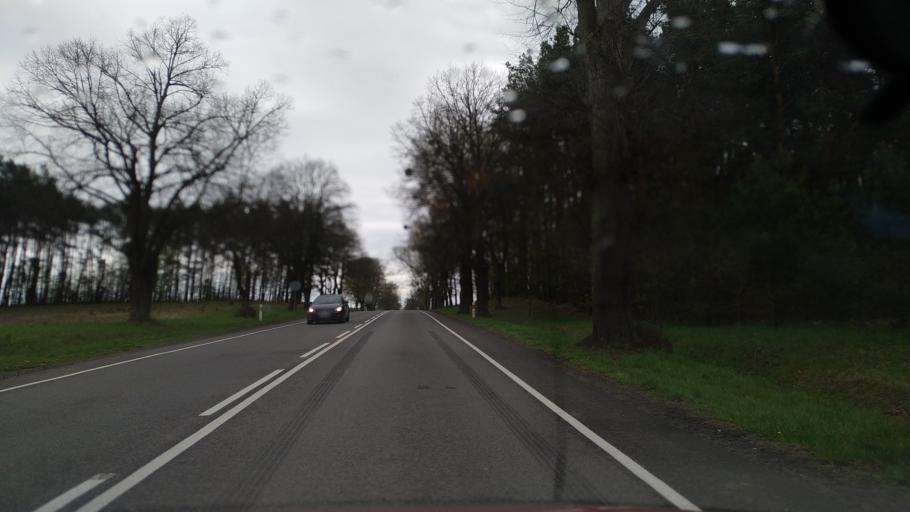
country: PL
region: Pomeranian Voivodeship
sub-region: Powiat starogardzki
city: Zblewo
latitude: 53.9321
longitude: 18.3557
